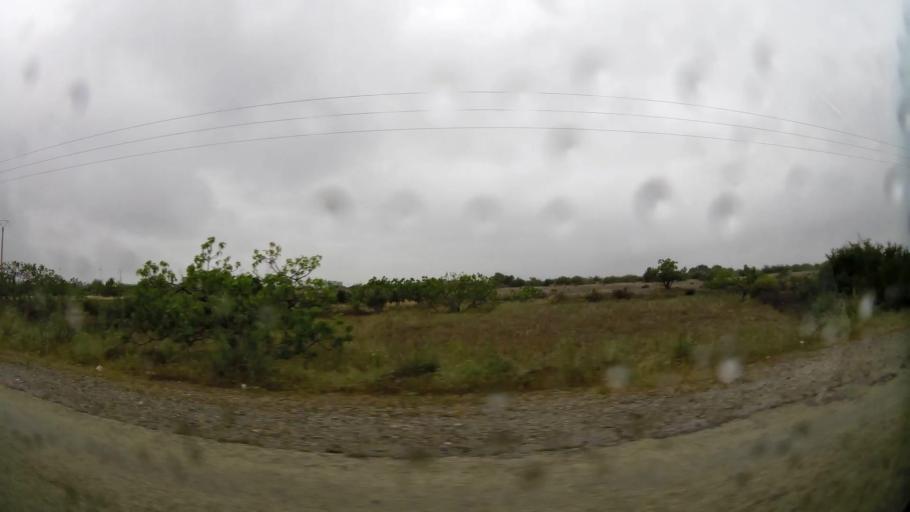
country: MA
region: Taza-Al Hoceima-Taounate
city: Imzourene
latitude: 35.1349
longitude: -3.7825
